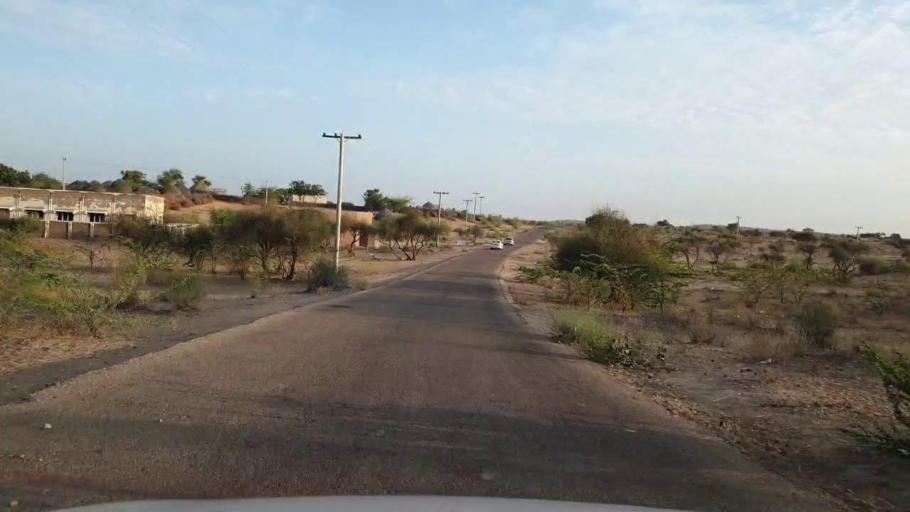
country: PK
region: Sindh
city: Nabisar
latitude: 25.0564
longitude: 69.9666
